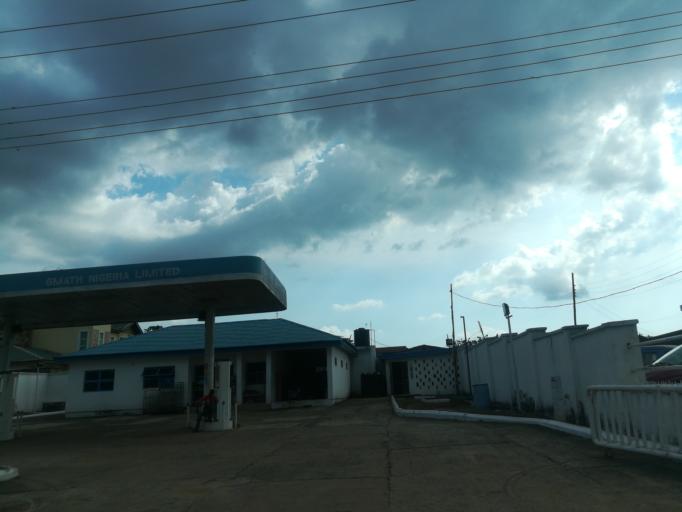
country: NG
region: Oyo
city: Ibadan
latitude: 7.4104
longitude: 3.8377
